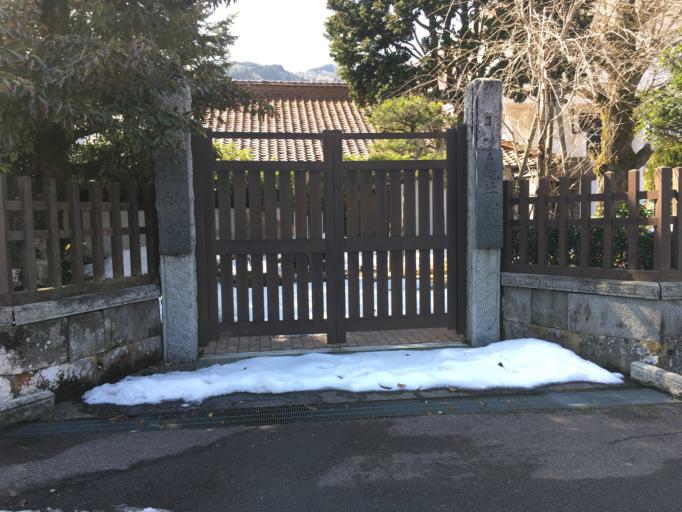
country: JP
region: Shimane
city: Masuda
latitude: 34.4547
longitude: 131.7668
